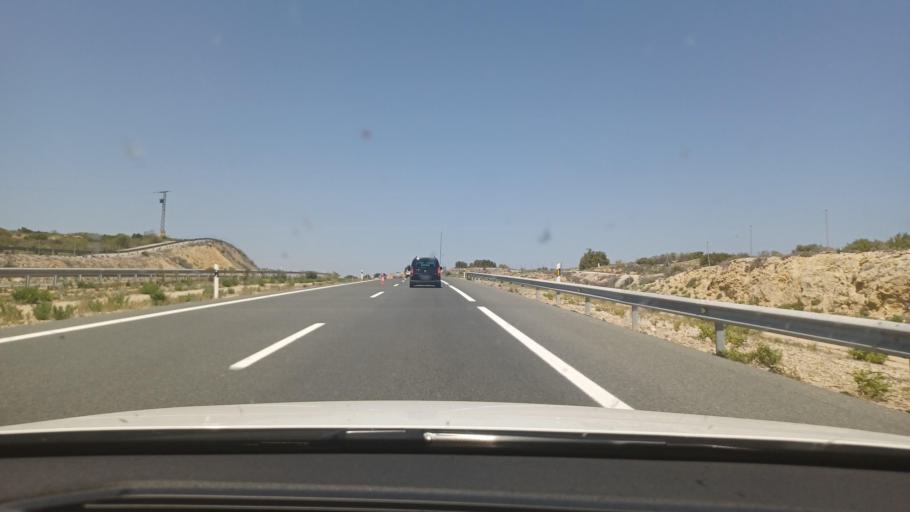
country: ES
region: Castille-La Mancha
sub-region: Provincia de Albacete
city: Alpera
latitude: 38.8791
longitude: -1.1982
